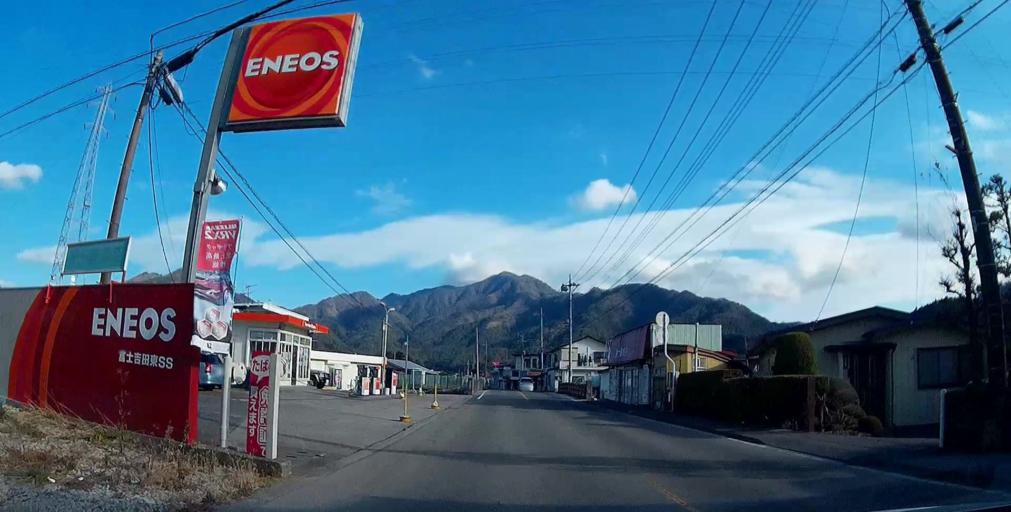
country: JP
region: Yamanashi
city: Fujikawaguchiko
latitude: 35.4956
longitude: 138.8187
